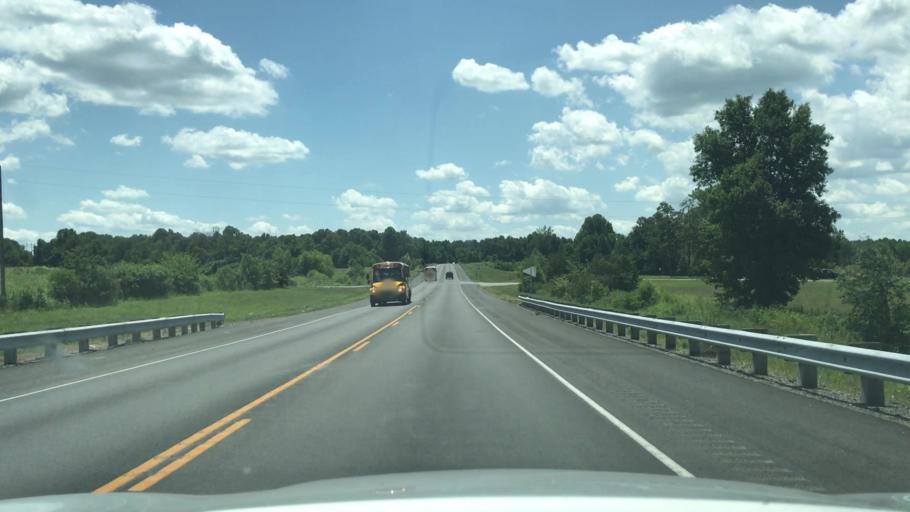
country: US
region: Kentucky
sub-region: Muhlenberg County
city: Greenville
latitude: 37.2112
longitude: -87.1926
